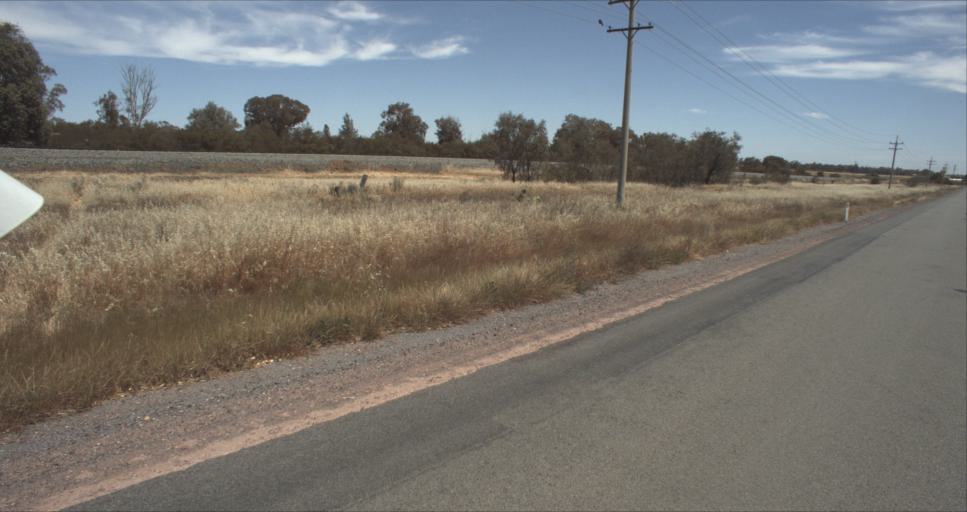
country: AU
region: New South Wales
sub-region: Leeton
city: Leeton
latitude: -34.6132
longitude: 146.4290
